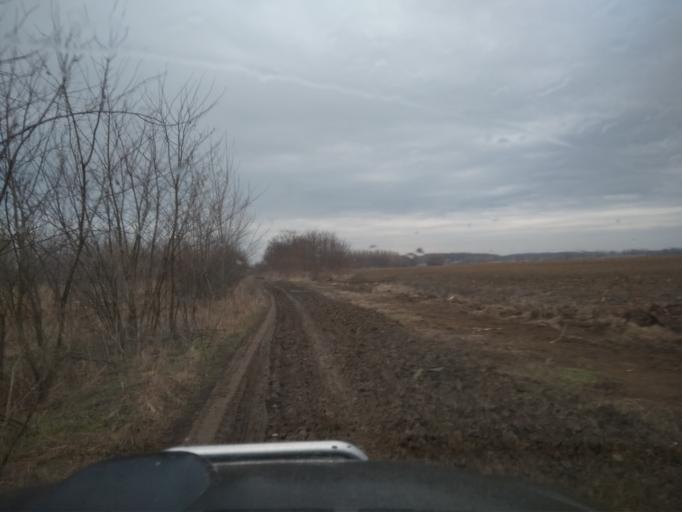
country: HU
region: Szabolcs-Szatmar-Bereg
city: Apagy
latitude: 47.9718
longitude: 21.9200
